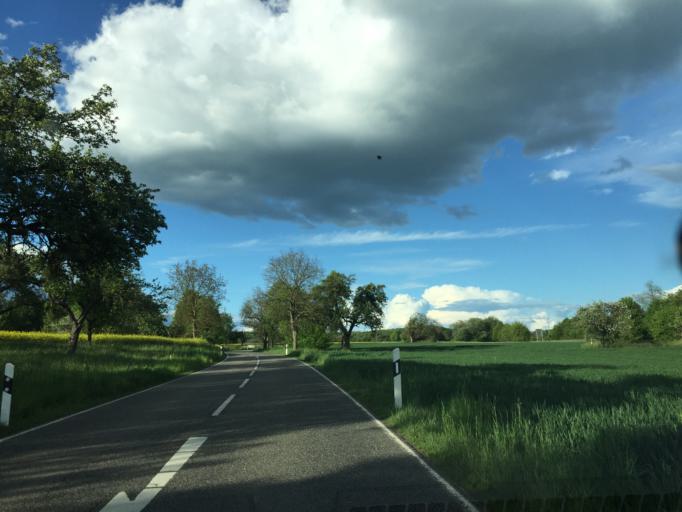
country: DE
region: Rheinland-Pfalz
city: Weitersburg
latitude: 50.4223
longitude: 7.6131
